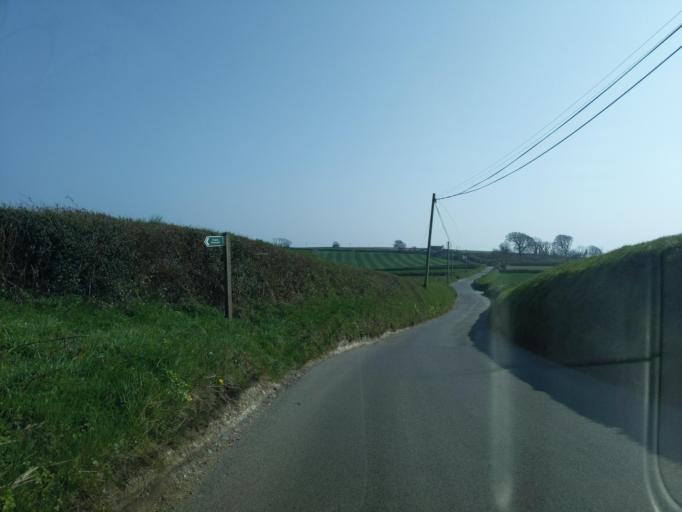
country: GB
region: England
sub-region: Devon
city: Dartmouth
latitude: 50.3496
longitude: -3.6588
